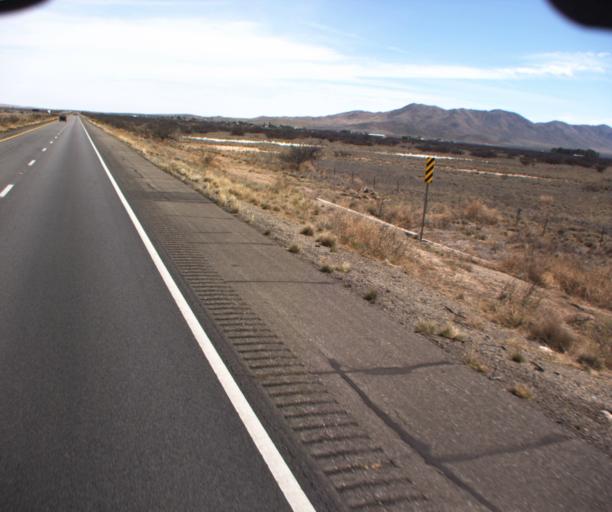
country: US
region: Arizona
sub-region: Cochise County
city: Willcox
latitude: 32.2852
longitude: -109.8244
